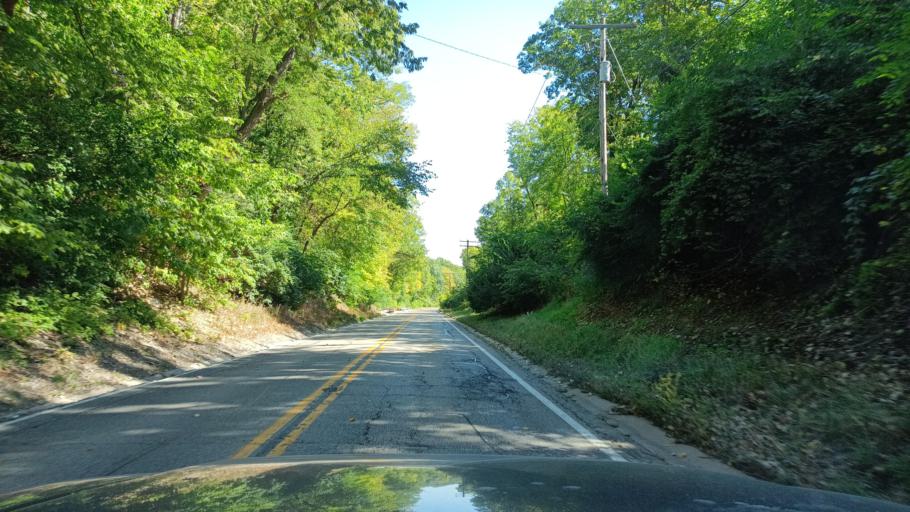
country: US
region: Illinois
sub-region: Woodford County
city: Eureka
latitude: 40.6274
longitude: -89.2520
